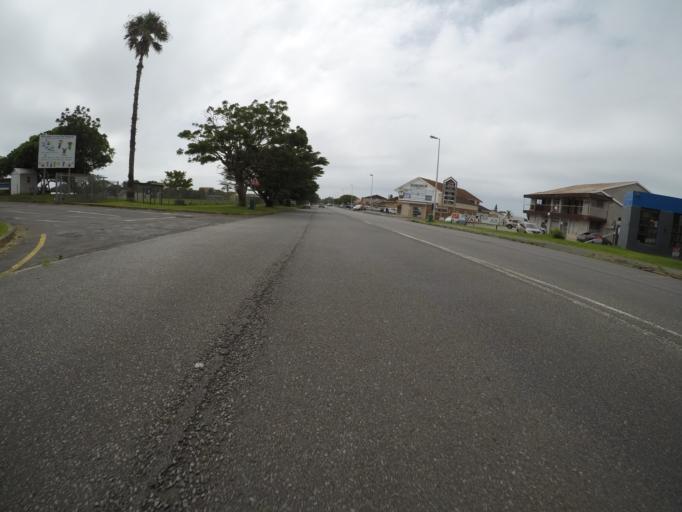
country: ZA
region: Eastern Cape
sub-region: Buffalo City Metropolitan Municipality
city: East London
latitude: -32.9381
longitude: 28.0099
